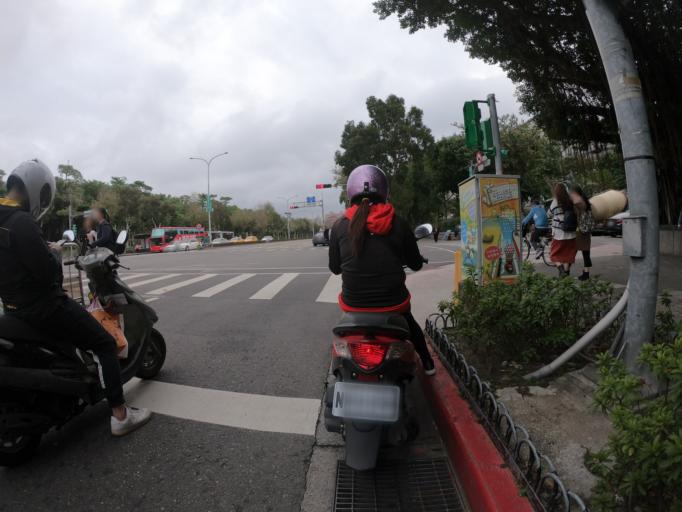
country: TW
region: Taipei
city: Taipei
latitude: 25.0308
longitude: 121.5335
